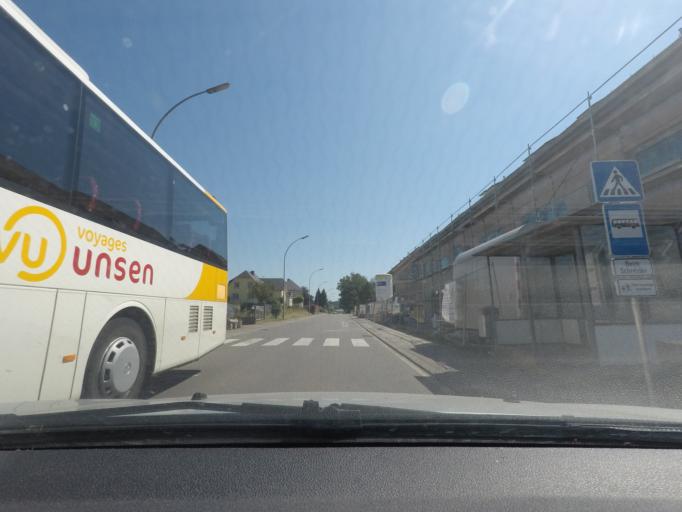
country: LU
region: Diekirch
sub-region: Canton de Redange
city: Ell
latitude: 49.7633
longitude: 5.8591
